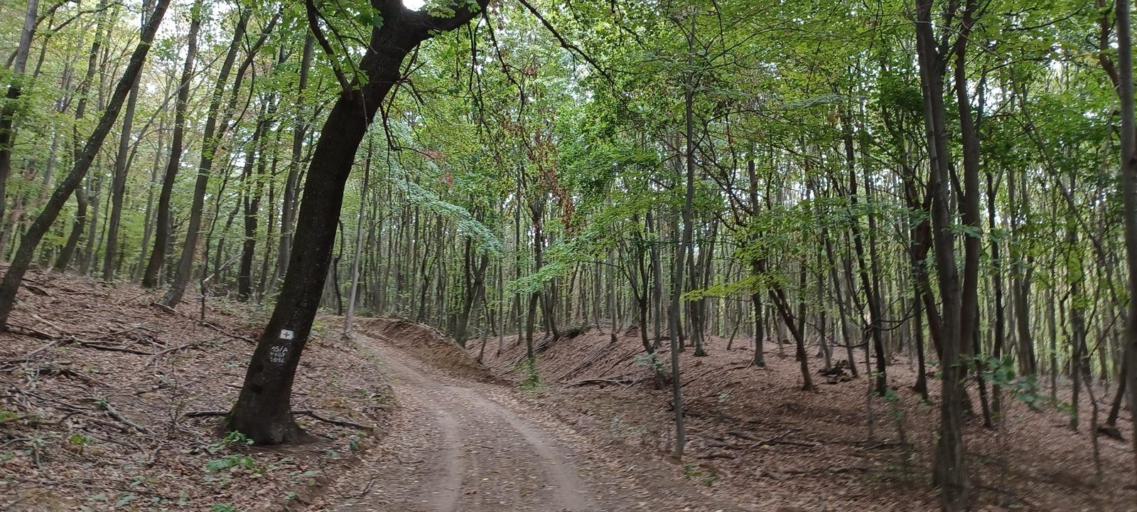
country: HU
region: Tolna
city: Szentgalpuszta
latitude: 46.3239
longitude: 18.6360
